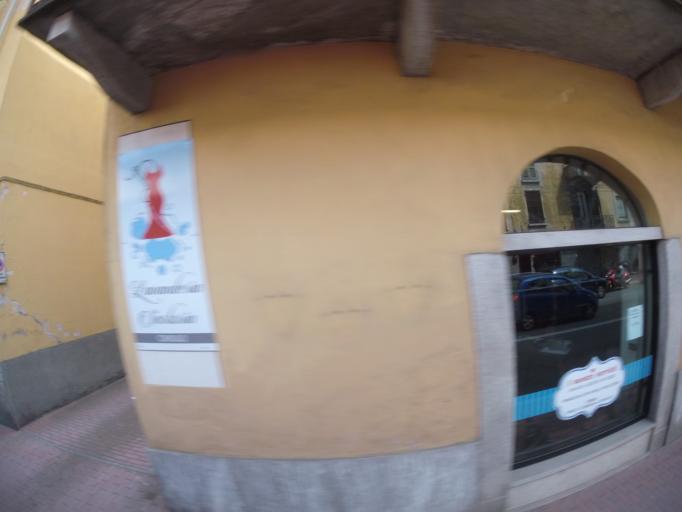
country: IT
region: Piedmont
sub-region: Provincia Verbano-Cusio-Ossola
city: Omegna
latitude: 45.8785
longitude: 8.4111
